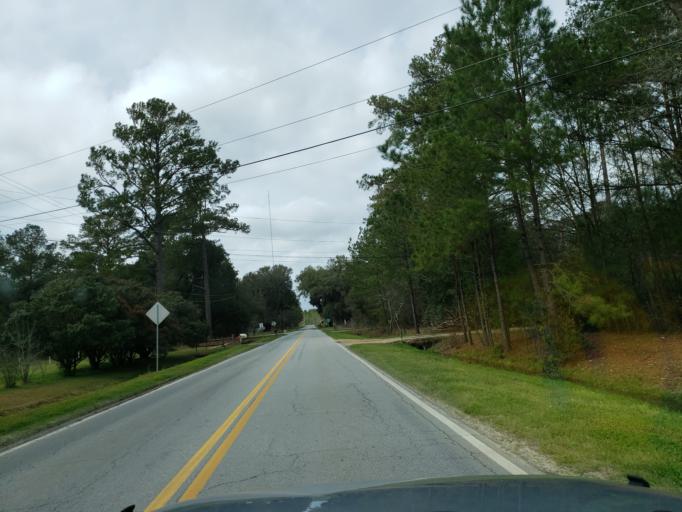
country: US
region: Georgia
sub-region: Chatham County
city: Pooler
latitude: 32.0483
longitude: -81.2852
